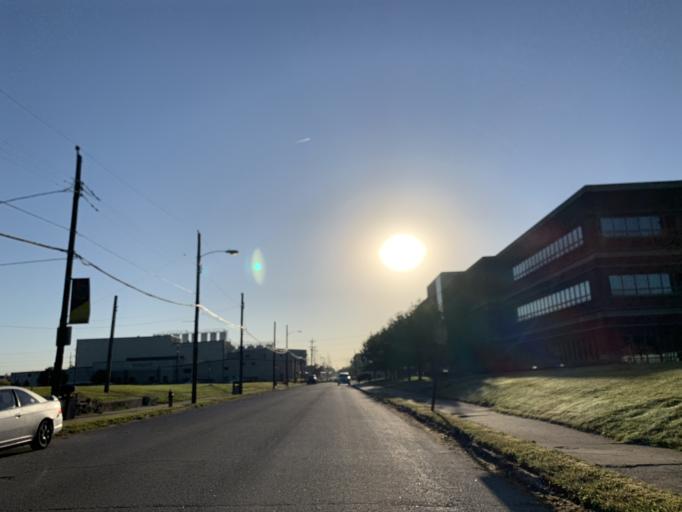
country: US
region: Kentucky
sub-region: Jefferson County
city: Louisville
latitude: 38.2415
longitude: -85.7795
